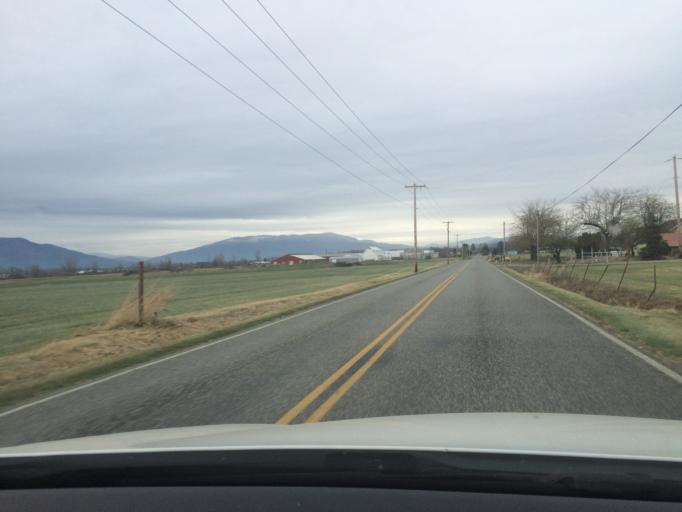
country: US
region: Washington
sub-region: Whatcom County
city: Everson
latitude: 48.9396
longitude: -122.3524
